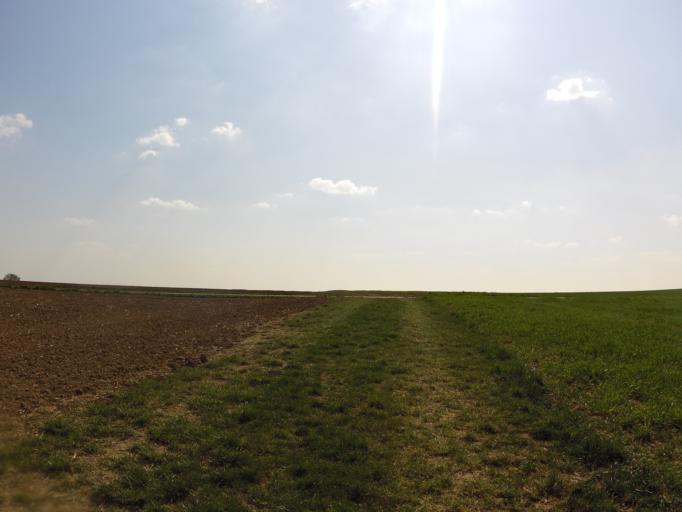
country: DE
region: Bavaria
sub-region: Regierungsbezirk Unterfranken
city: Dettelbach
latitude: 49.8161
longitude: 10.1470
